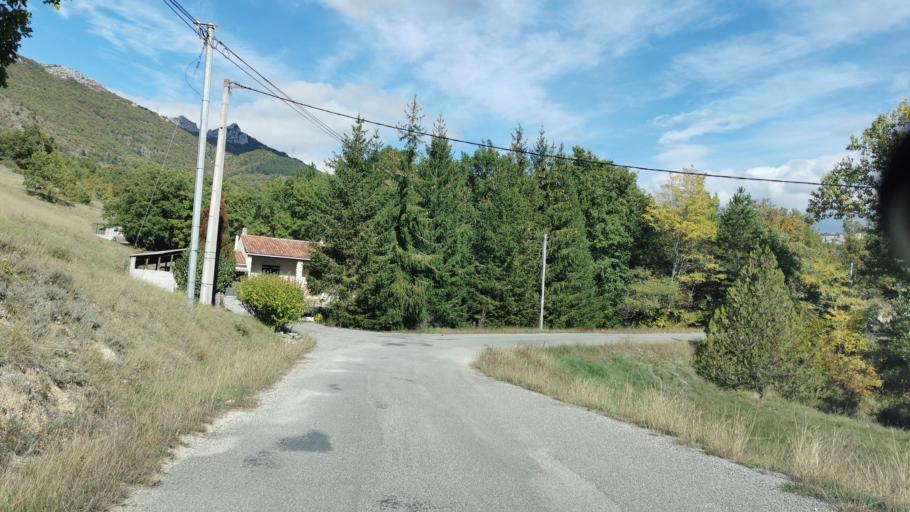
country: FR
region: Provence-Alpes-Cote d'Azur
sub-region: Departement des Alpes-de-Haute-Provence
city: Sisteron
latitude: 44.1864
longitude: 6.0095
